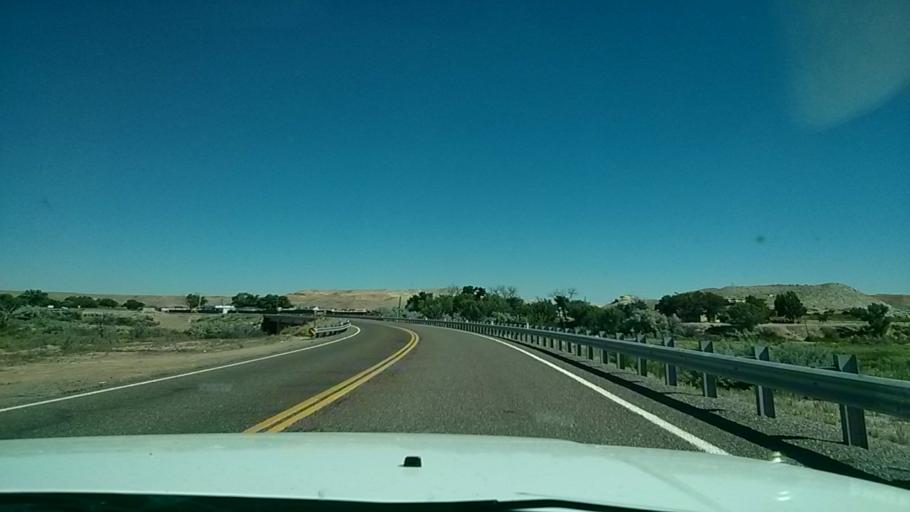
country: US
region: Utah
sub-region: Emery County
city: Ferron
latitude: 38.3762
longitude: -110.7311
